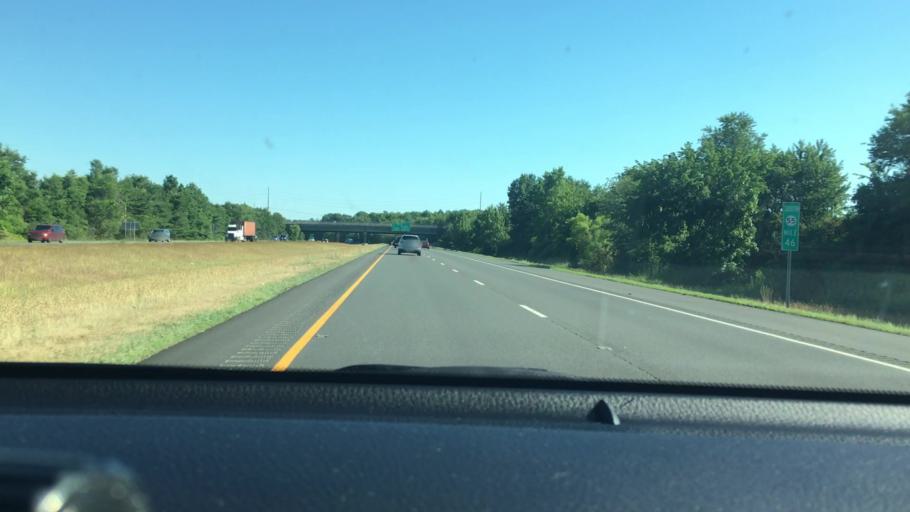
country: US
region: New Jersey
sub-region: Gloucester County
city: Clayton
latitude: 39.6614
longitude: -75.1266
